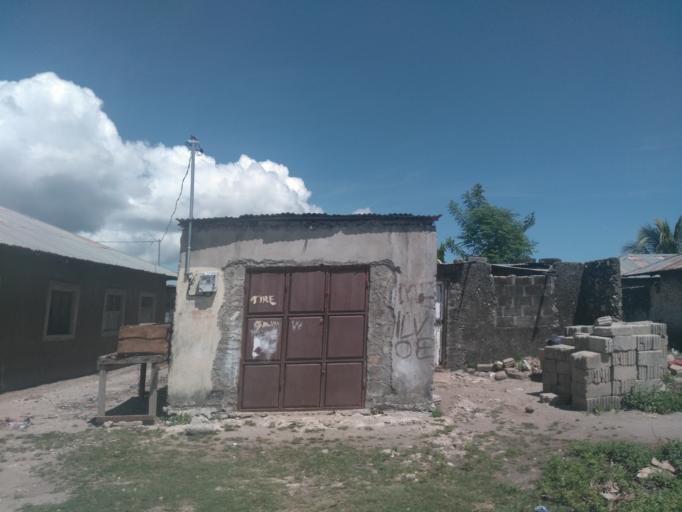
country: TZ
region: Zanzibar North
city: Gamba
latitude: -5.9245
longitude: 39.3557
